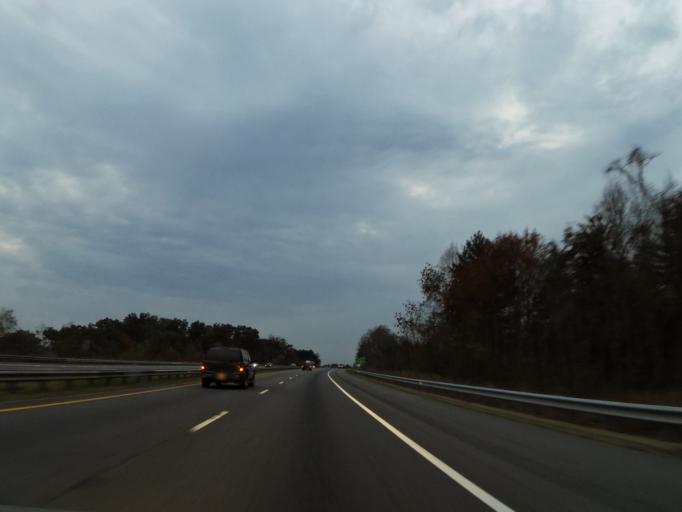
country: US
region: North Carolina
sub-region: McDowell County
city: Marion
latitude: 35.6866
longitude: -81.9029
